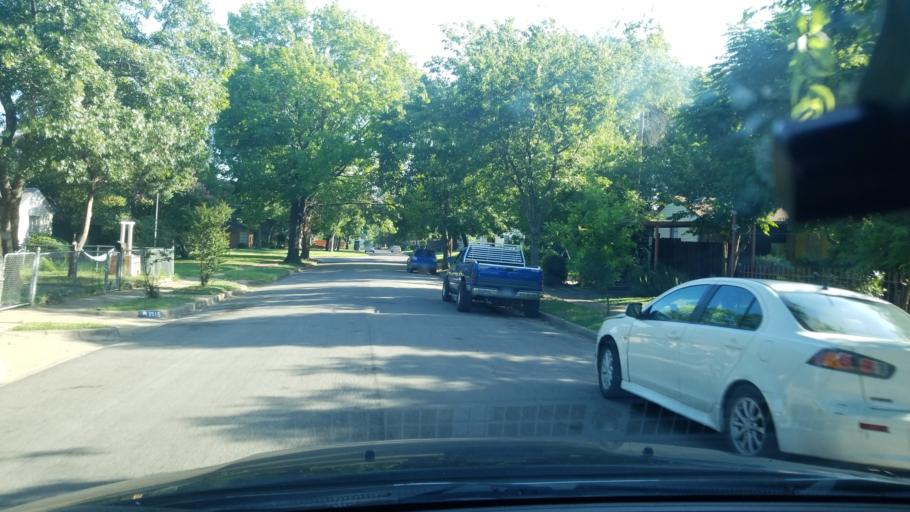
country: US
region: Texas
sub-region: Dallas County
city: Dallas
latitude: 32.7287
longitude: -96.8168
